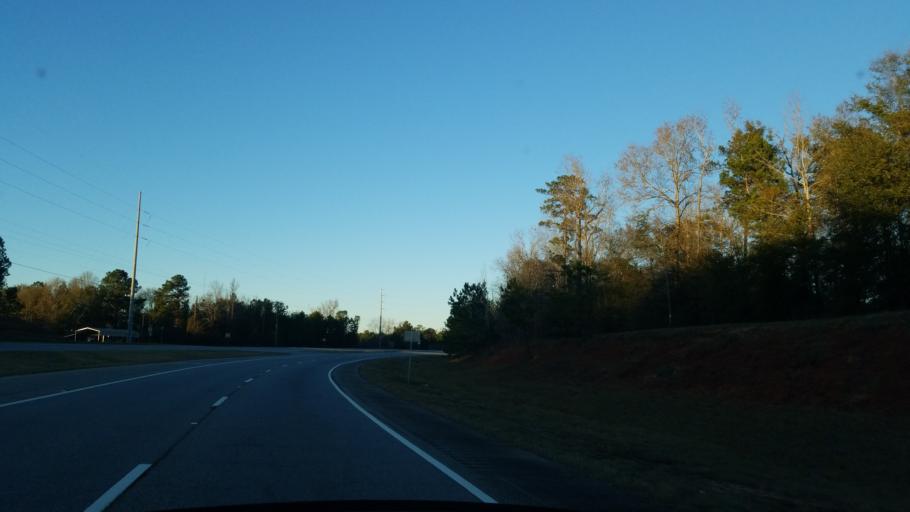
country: US
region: Georgia
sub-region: Chattahoochee County
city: Cusseta
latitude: 32.2790
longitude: -84.7812
